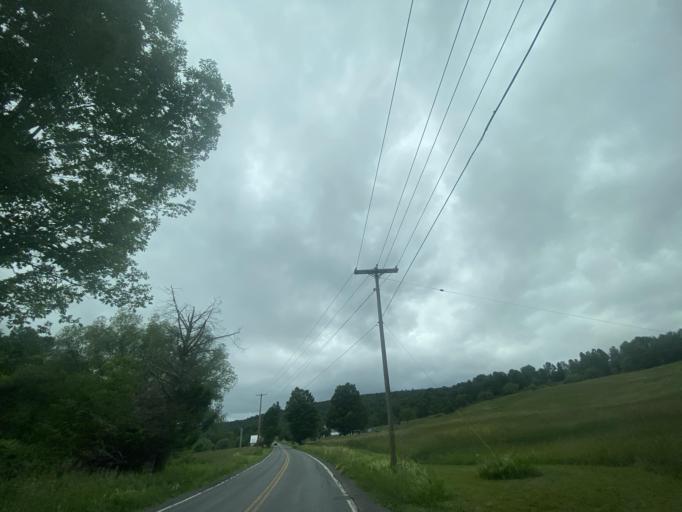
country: US
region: New York
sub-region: Schoharie County
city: Middleburgh
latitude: 42.3869
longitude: -74.3678
